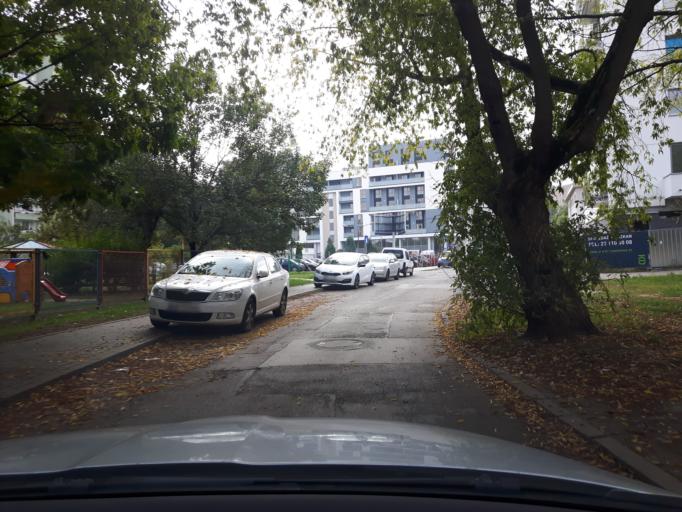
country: PL
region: Masovian Voivodeship
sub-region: Warszawa
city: Targowek
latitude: 52.2711
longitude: 21.0488
